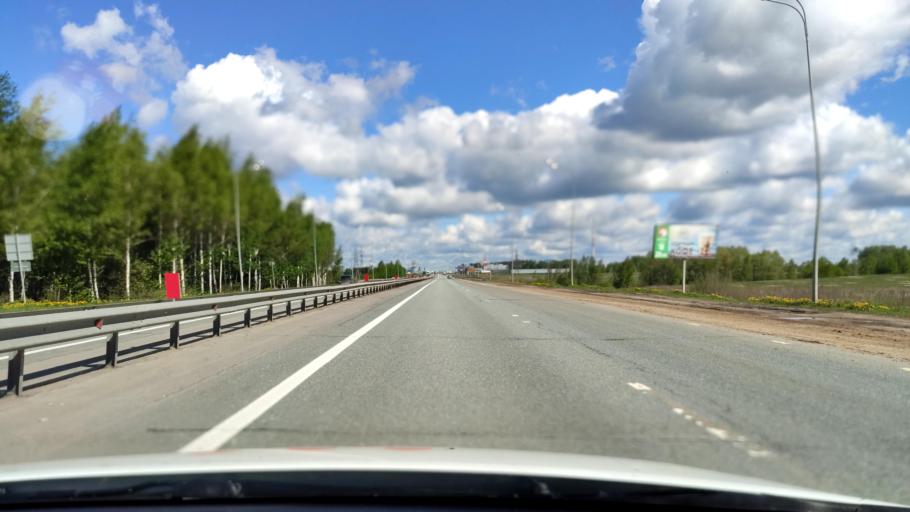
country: RU
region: Tatarstan
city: Osinovo
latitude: 55.8684
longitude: 48.8568
